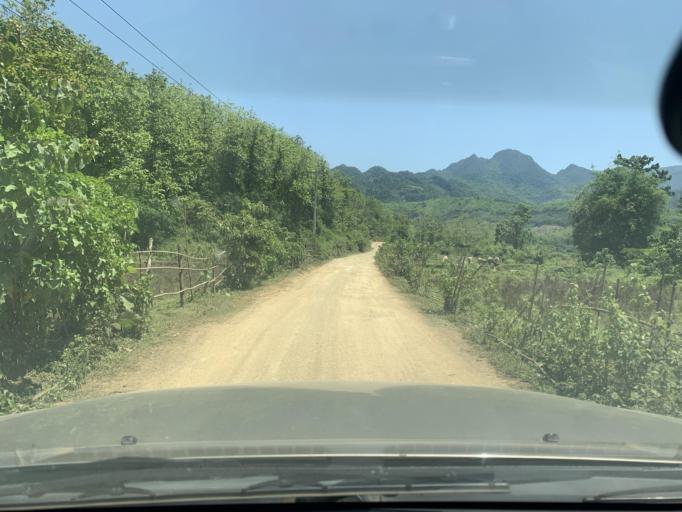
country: LA
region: Louangphabang
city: Louangphabang
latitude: 19.9046
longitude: 102.2500
